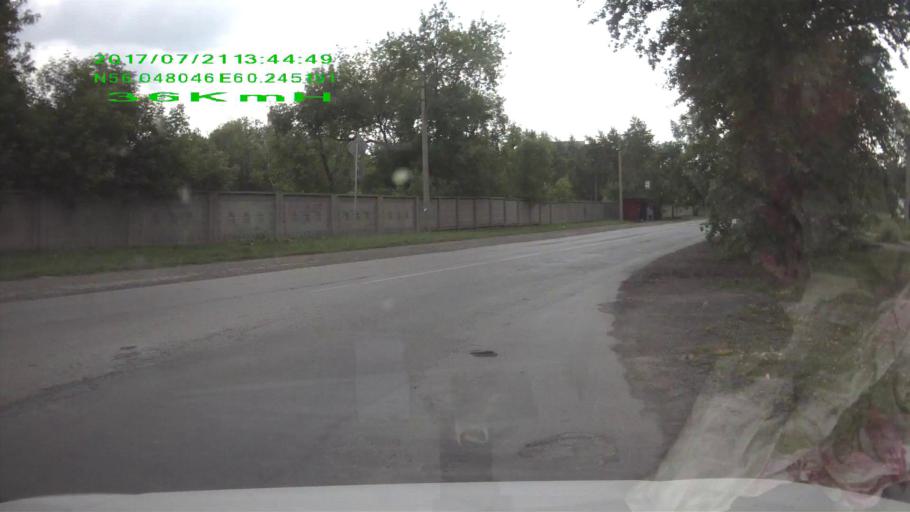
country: RU
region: Chelyabinsk
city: Verkhniy Ufaley
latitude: 56.0477
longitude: 60.2453
